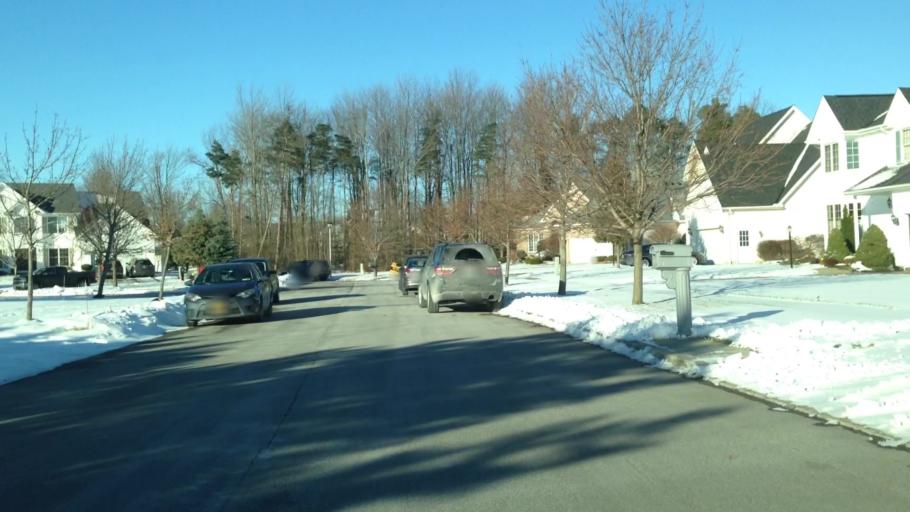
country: US
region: New York
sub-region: Erie County
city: Lancaster
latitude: 42.8668
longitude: -78.6844
